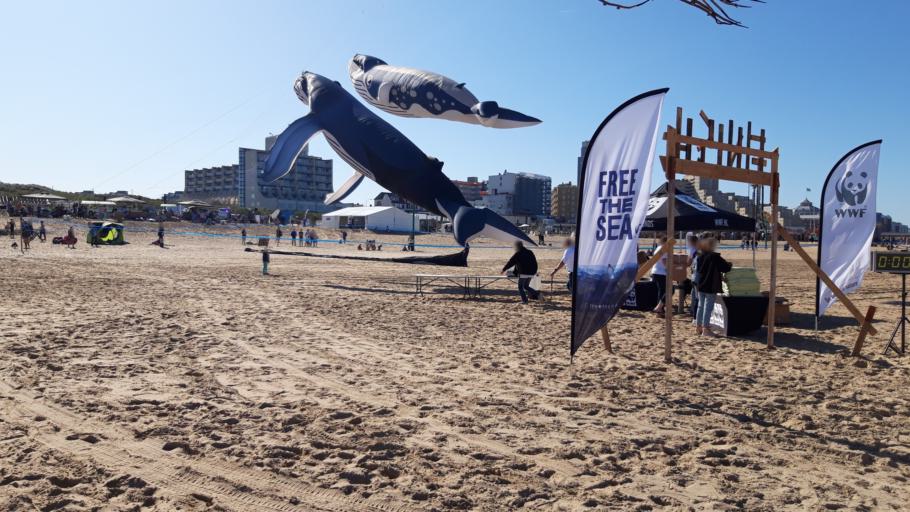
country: NL
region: South Holland
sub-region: Gemeente Den Haag
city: Scheveningen
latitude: 52.1194
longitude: 4.2871
